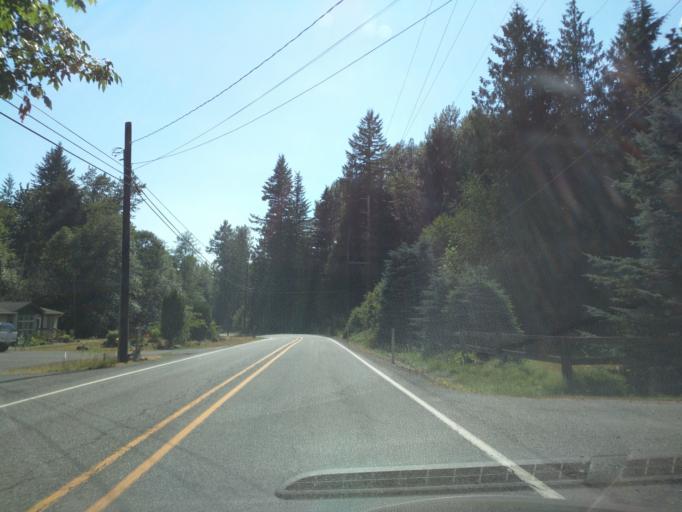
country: US
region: Washington
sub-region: Whatcom County
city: Peaceful Valley
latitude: 48.9203
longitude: -122.0972
